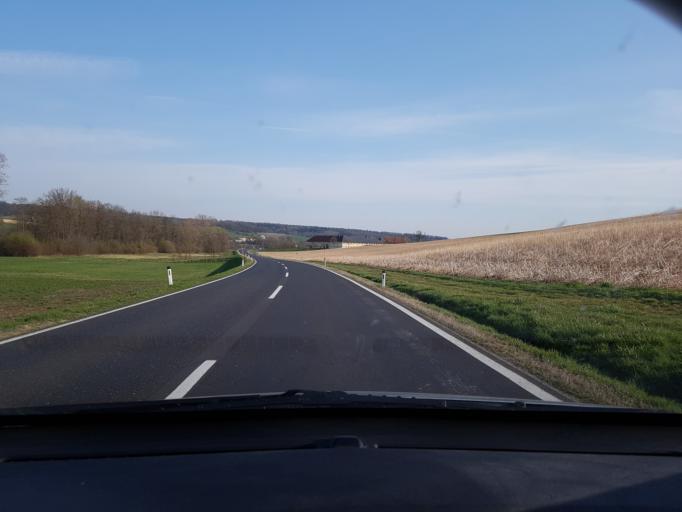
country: AT
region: Upper Austria
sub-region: Politischer Bezirk Linz-Land
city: Sankt Florian
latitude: 48.1836
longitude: 14.3456
